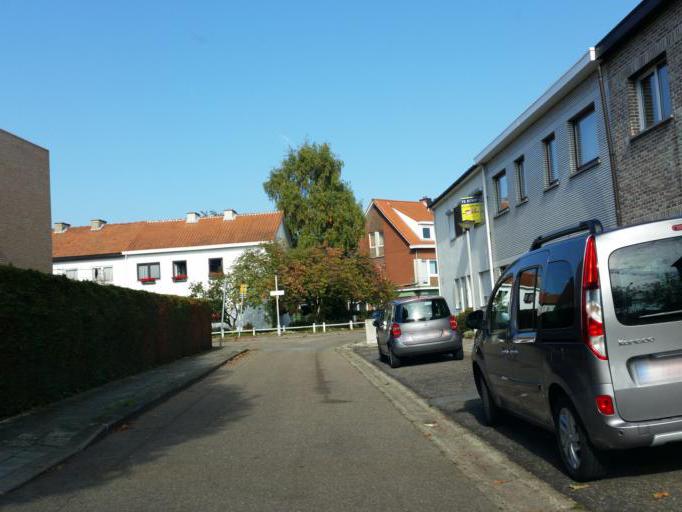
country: BE
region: Flanders
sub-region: Provincie Antwerpen
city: Aartselaar
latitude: 51.1521
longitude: 4.3864
